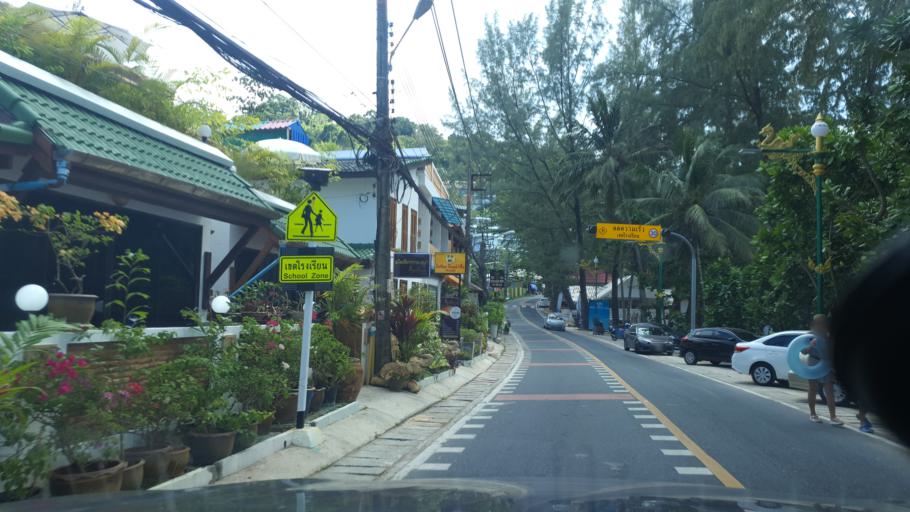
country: TH
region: Phuket
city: Thalang
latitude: 8.0569
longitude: 98.2783
